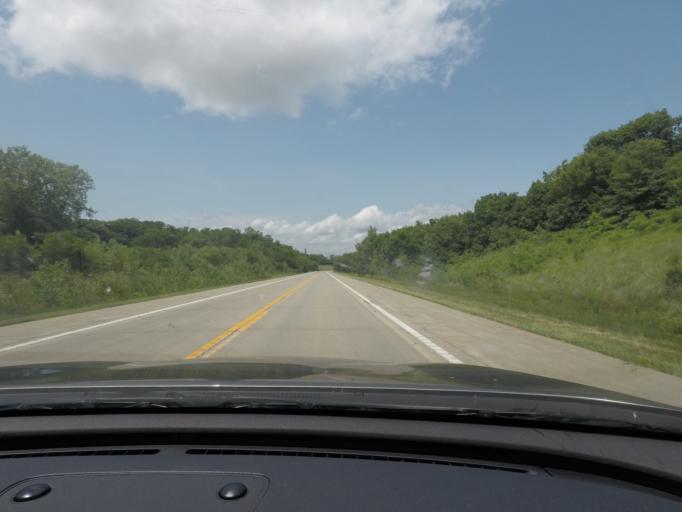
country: US
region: Missouri
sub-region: Carroll County
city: Carrollton
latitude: 39.2081
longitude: -93.5073
